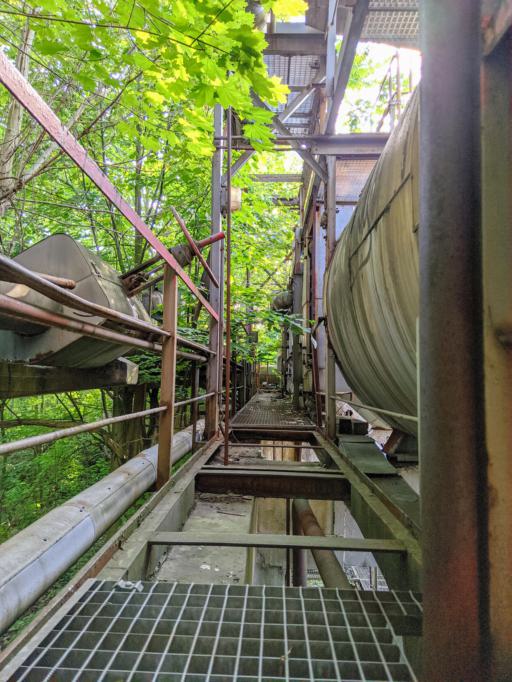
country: DE
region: Brandenburg
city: Cottbus
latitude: 51.7511
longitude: 14.3379
